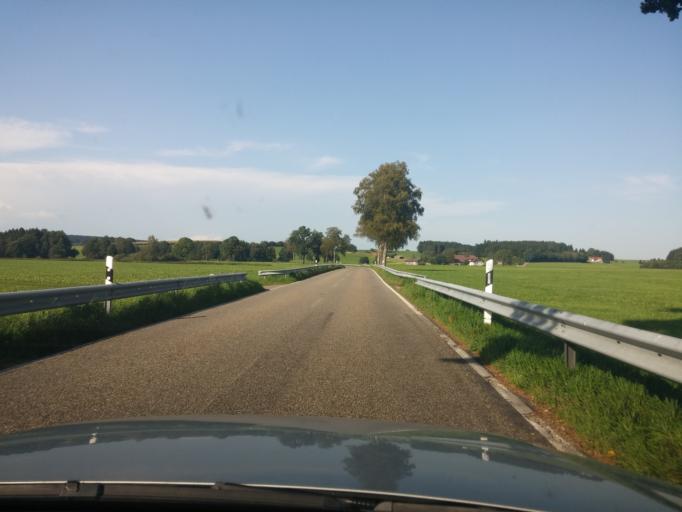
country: DE
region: Baden-Wuerttemberg
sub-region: Tuebingen Region
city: Leutkirch im Allgau
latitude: 47.8211
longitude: 10.0614
